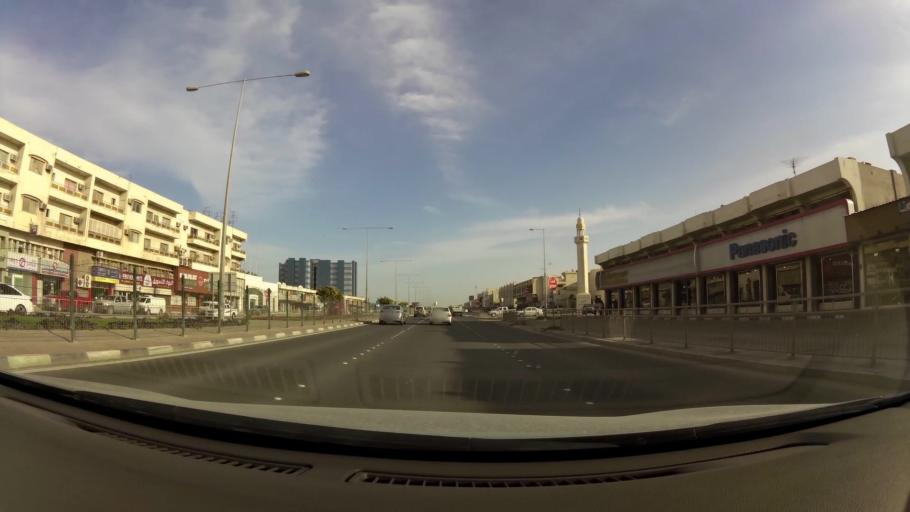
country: QA
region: Al Wakrah
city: Al Wakrah
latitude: 25.1824
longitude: 51.6018
